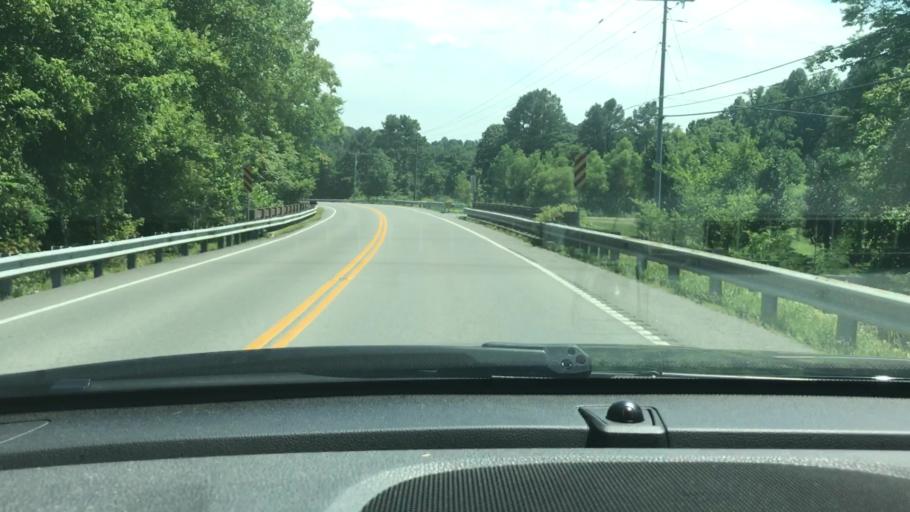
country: US
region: Tennessee
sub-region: Sumner County
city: Shackle Island
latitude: 36.4068
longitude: -86.6342
